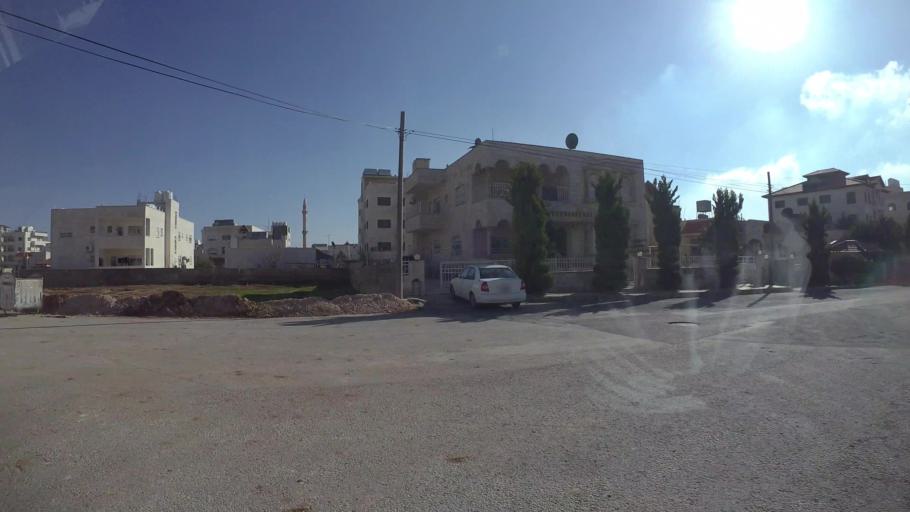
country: JO
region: Amman
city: Al Bunayyat ash Shamaliyah
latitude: 31.9024
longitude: 35.9185
